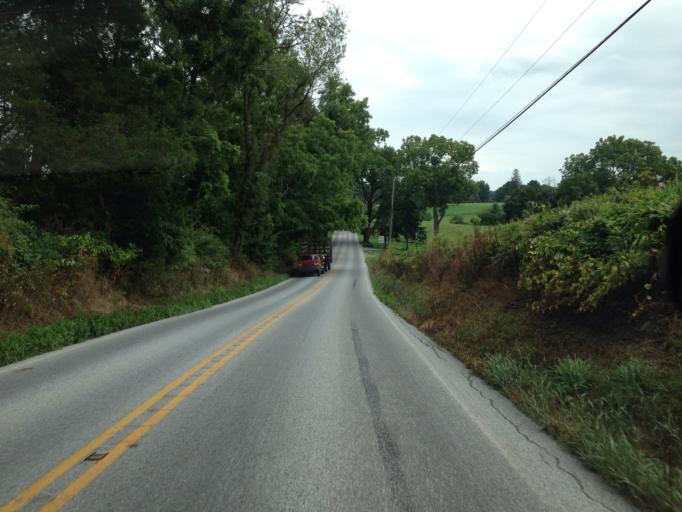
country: US
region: Pennsylvania
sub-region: Chester County
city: Oxford
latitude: 39.8634
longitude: -75.9915
